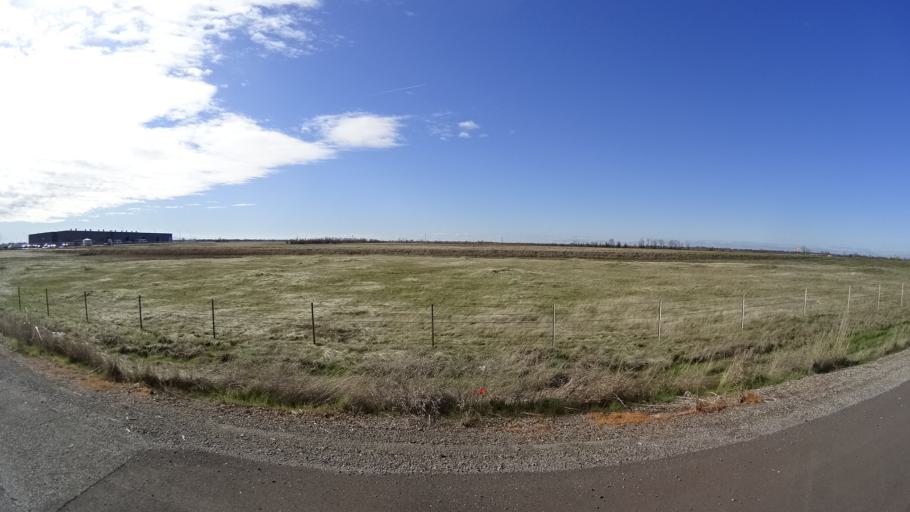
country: US
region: California
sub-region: Butte County
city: Durham
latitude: 39.6438
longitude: -121.7224
